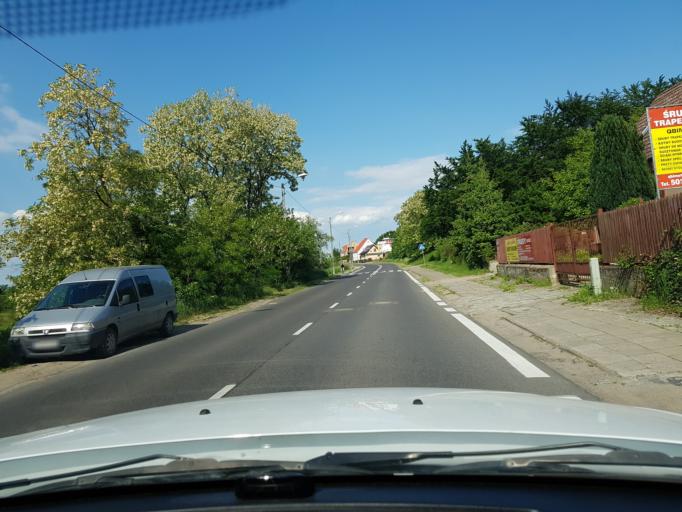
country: PL
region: West Pomeranian Voivodeship
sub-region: Szczecin
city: Szczecin
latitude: 53.3414
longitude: 14.5547
